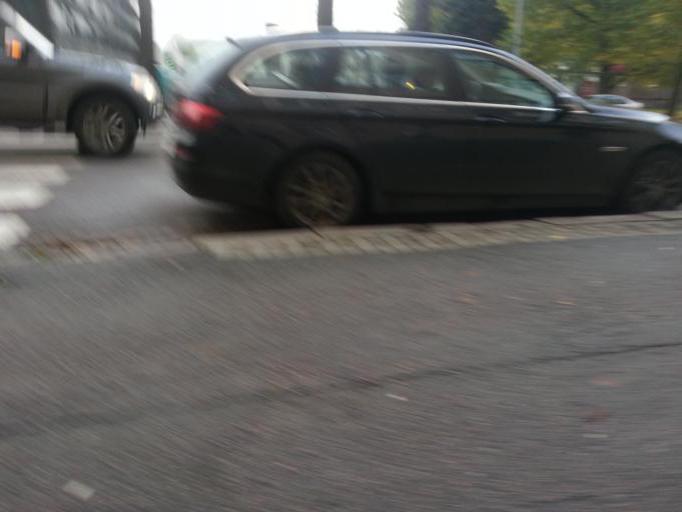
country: FI
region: Uusimaa
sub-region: Helsinki
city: Helsinki
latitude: 60.1893
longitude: 24.9561
